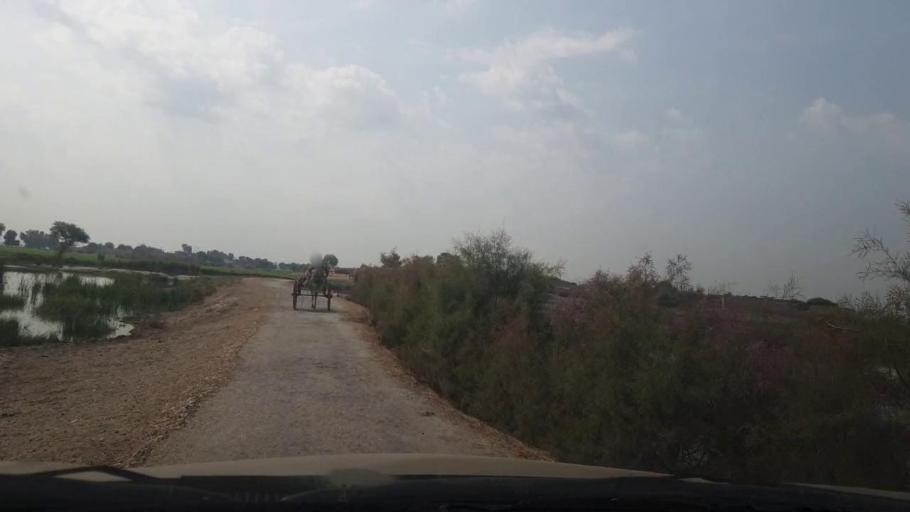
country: PK
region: Sindh
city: Larkana
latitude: 27.6510
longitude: 68.2097
